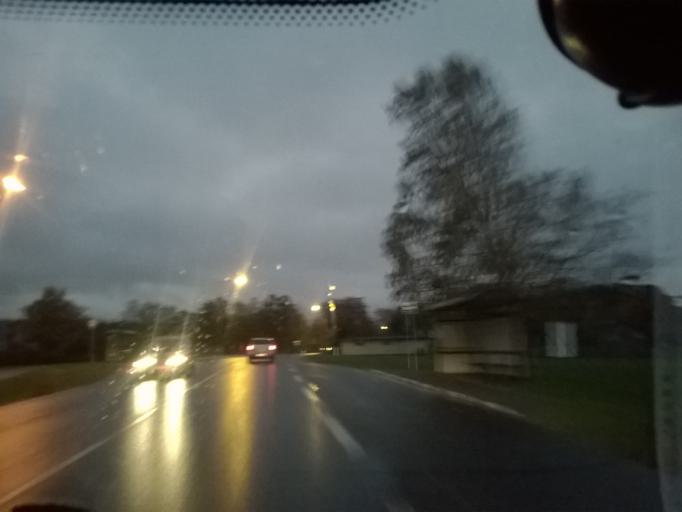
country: EE
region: Harju
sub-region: Viimsi vald
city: Rummu
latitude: 59.5318
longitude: 24.7953
